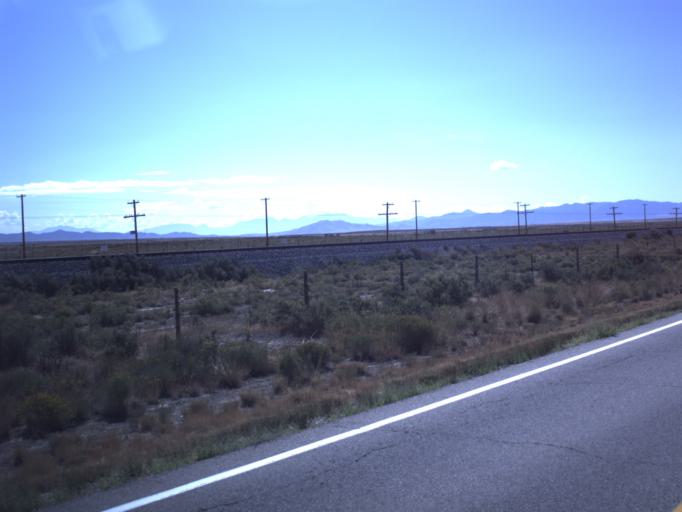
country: US
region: Utah
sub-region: Tooele County
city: Tooele
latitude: 40.2942
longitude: -112.4013
